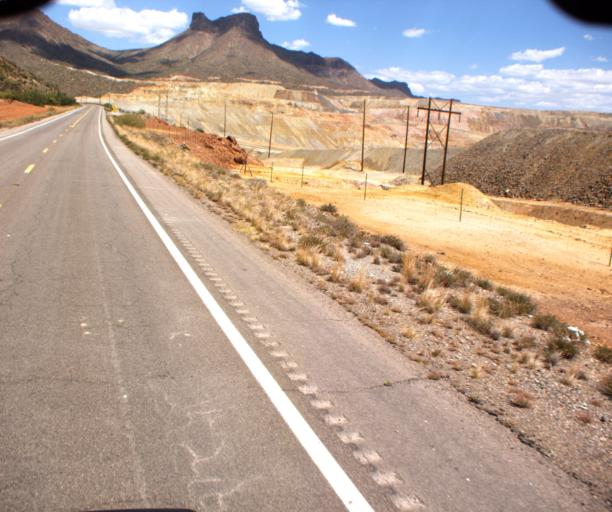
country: US
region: Arizona
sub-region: Pinal County
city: Kearny
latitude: 33.1686
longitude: -111.0085
